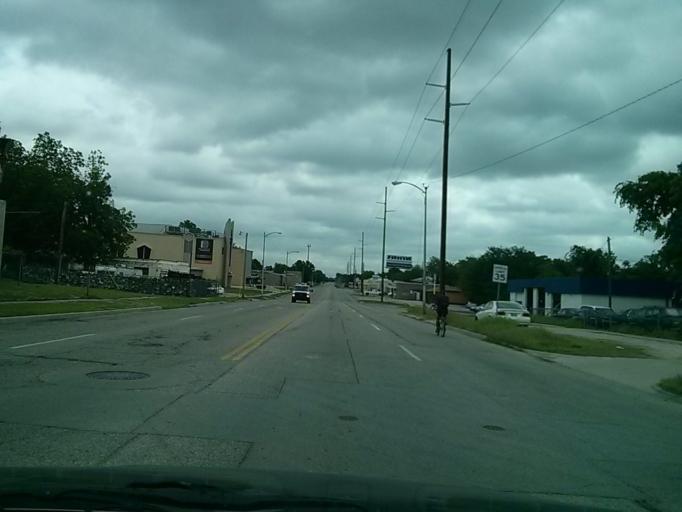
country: US
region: Oklahoma
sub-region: Tulsa County
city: Tulsa
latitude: 36.1566
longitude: -95.9661
